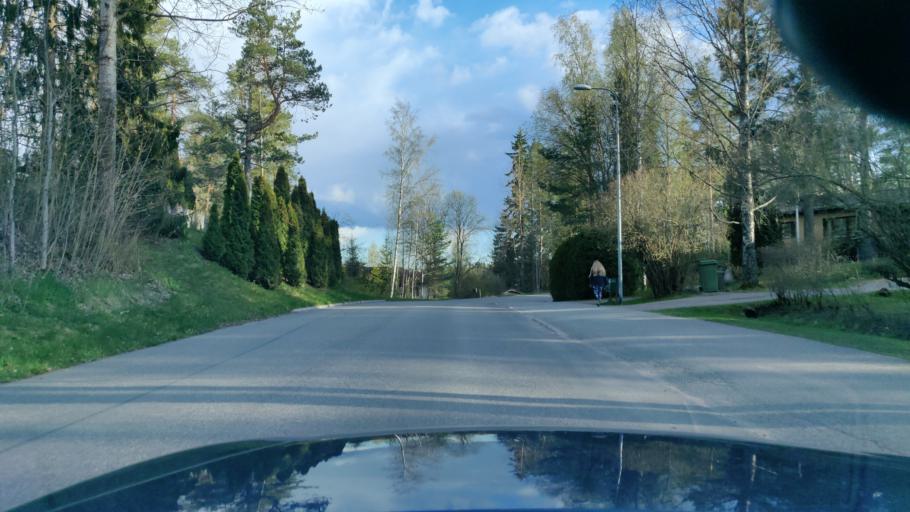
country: FI
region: Uusimaa
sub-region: Helsinki
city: Nurmijaervi
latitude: 60.3718
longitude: 24.7543
